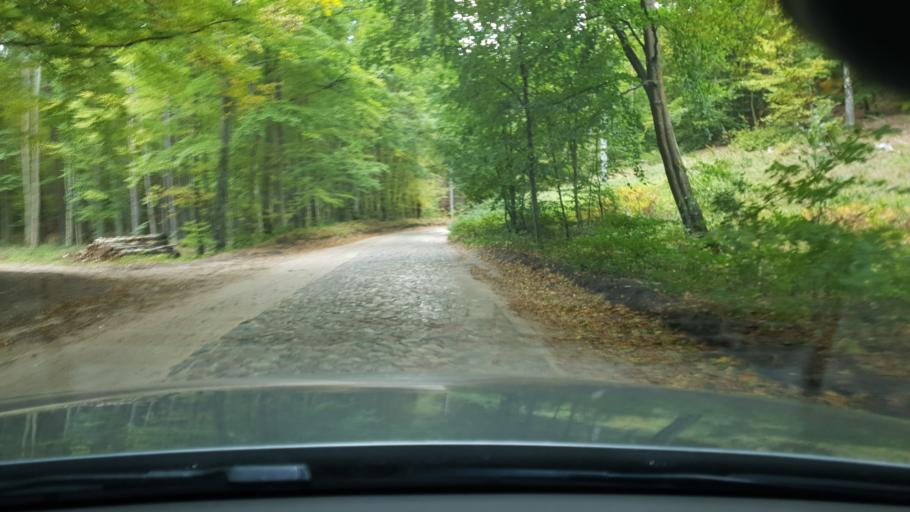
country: PL
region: Pomeranian Voivodeship
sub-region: Powiat wejherowski
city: Reda
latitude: 54.5884
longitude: 18.3256
